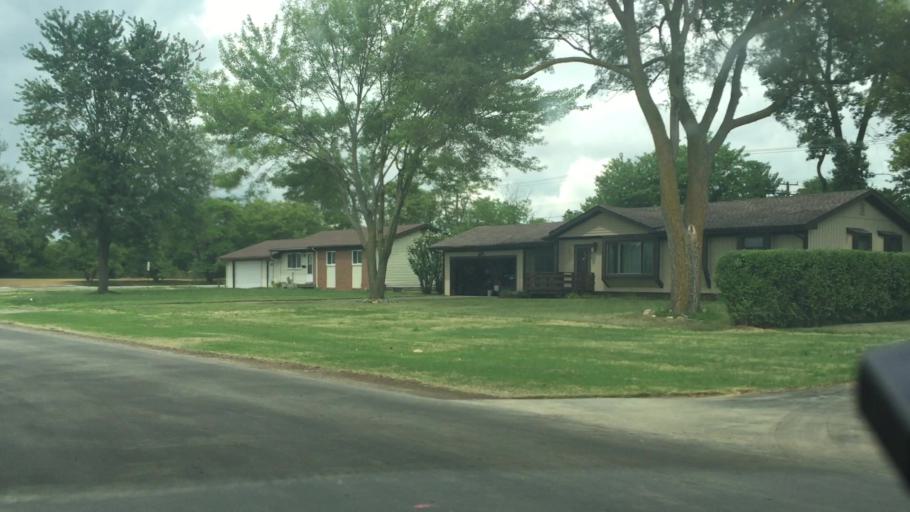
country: US
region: Michigan
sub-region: Oakland County
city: Auburn Hills
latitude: 42.6709
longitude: -83.2389
